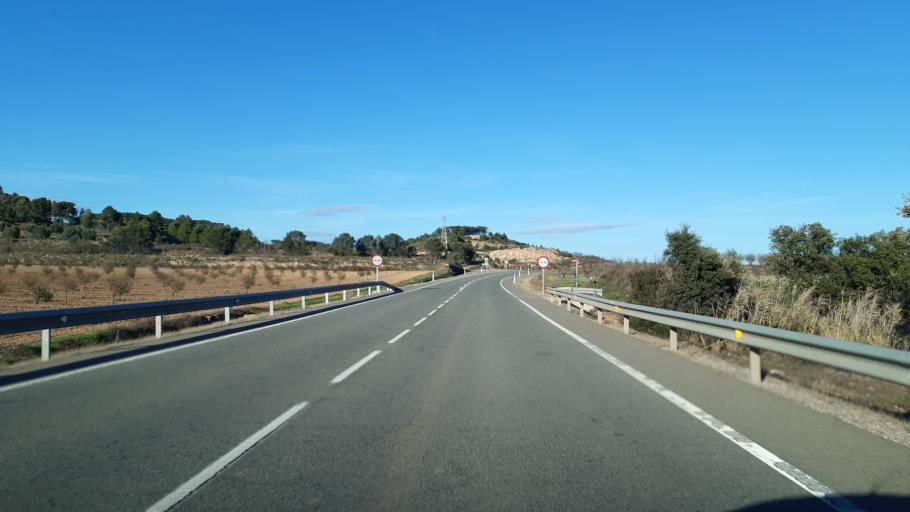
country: ES
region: Catalonia
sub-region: Provincia de Tarragona
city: la Fatarella
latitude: 41.0955
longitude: 0.5159
